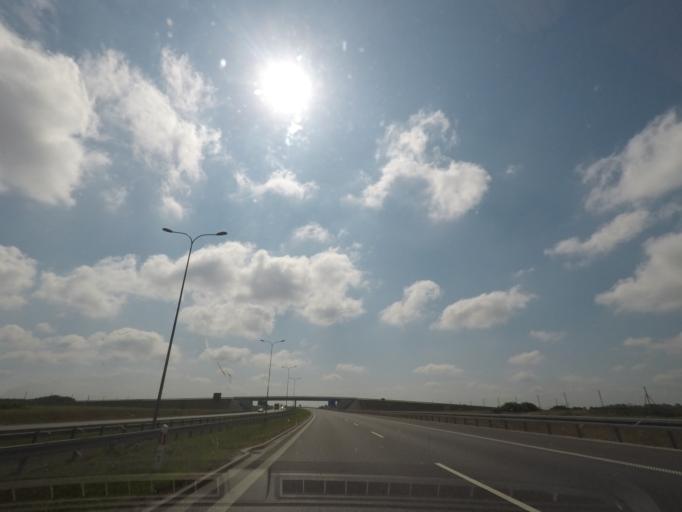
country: PL
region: Kujawsko-Pomorskie
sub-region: Powiat wloclawski
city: Brzesc Kujawski
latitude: 52.6136
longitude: 18.9703
